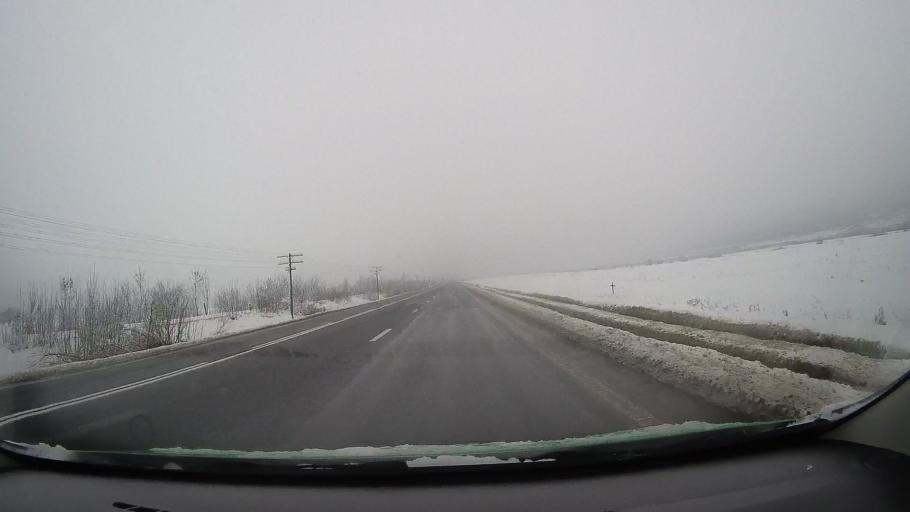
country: RO
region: Sibiu
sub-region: Oras Saliste
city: Saliste
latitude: 45.7963
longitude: 23.9097
